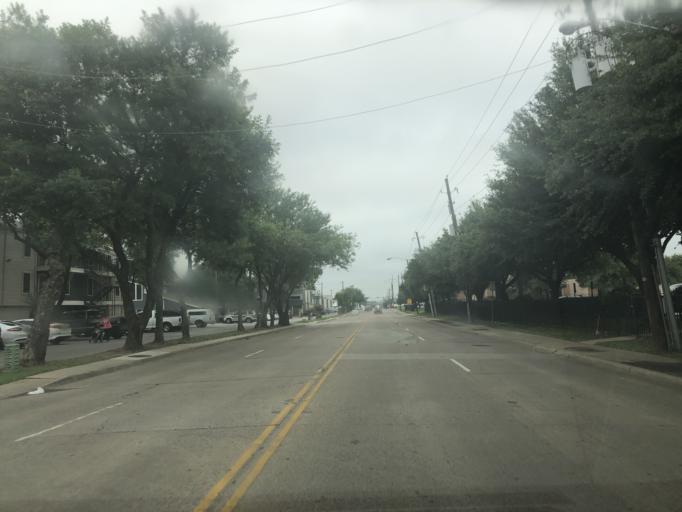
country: US
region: Texas
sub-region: Dallas County
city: Farmers Branch
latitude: 32.8665
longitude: -96.8722
